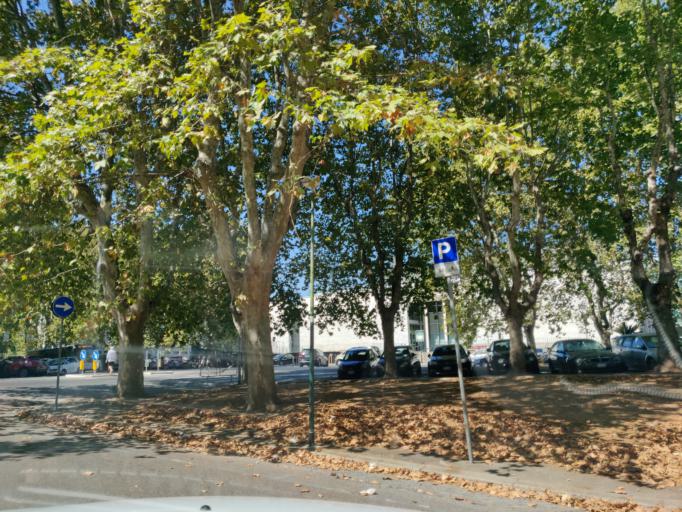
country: IT
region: Latium
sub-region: Citta metropolitana di Roma Capitale
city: Selcetta
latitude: 41.8332
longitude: 12.4672
